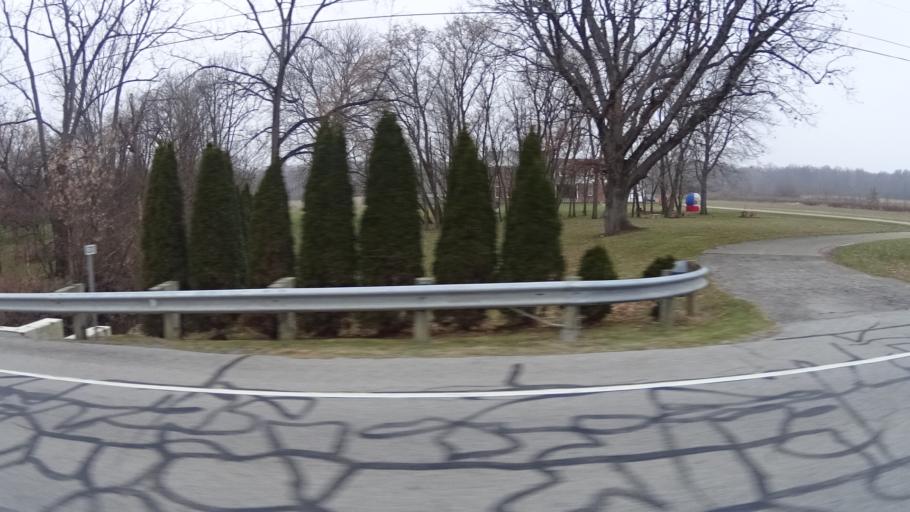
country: US
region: Ohio
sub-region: Lorain County
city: South Amherst
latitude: 41.3029
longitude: -82.2732
